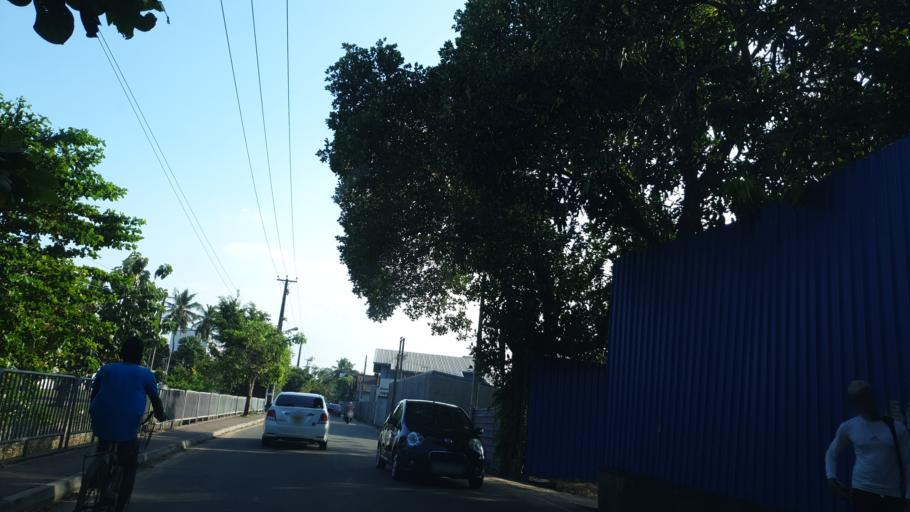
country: LK
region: Western
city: Galkissa
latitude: 6.8486
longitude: 79.8771
